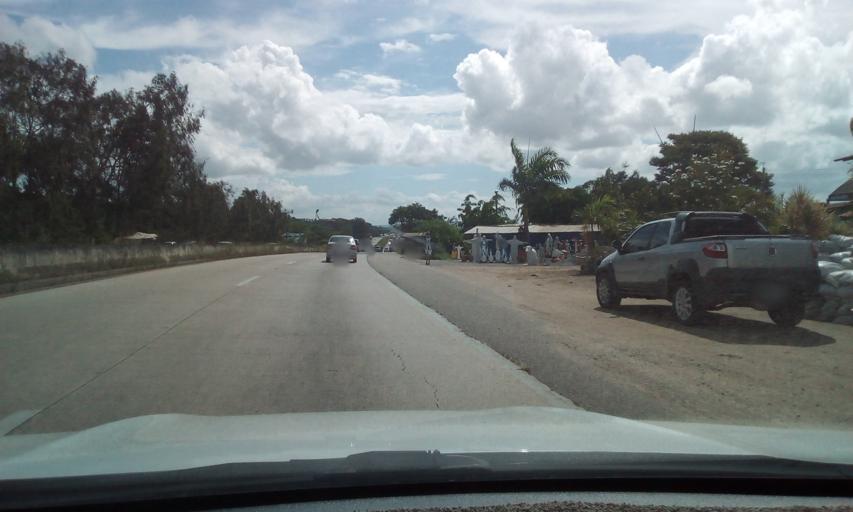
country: BR
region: Pernambuco
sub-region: Cha Grande
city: Cha Grande
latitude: -8.1872
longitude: -35.5012
